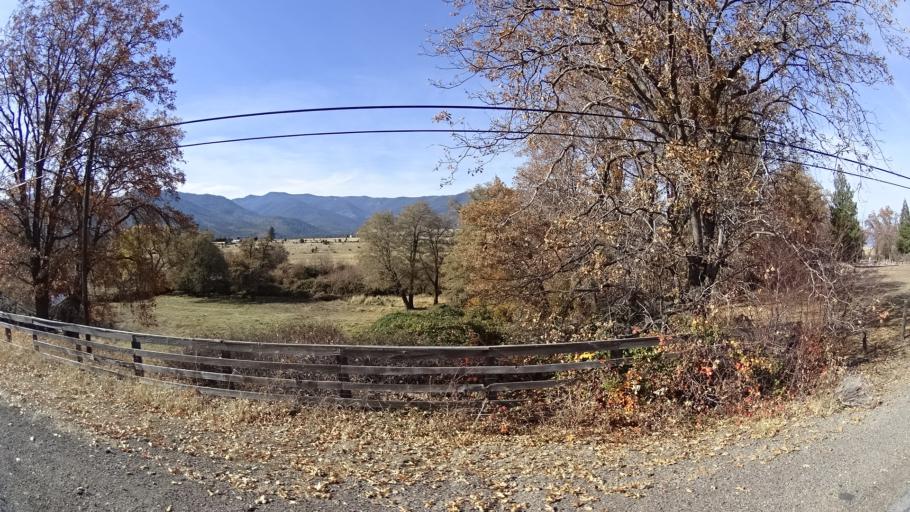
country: US
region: California
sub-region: Siskiyou County
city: Weed
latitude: 41.4507
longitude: -122.4307
